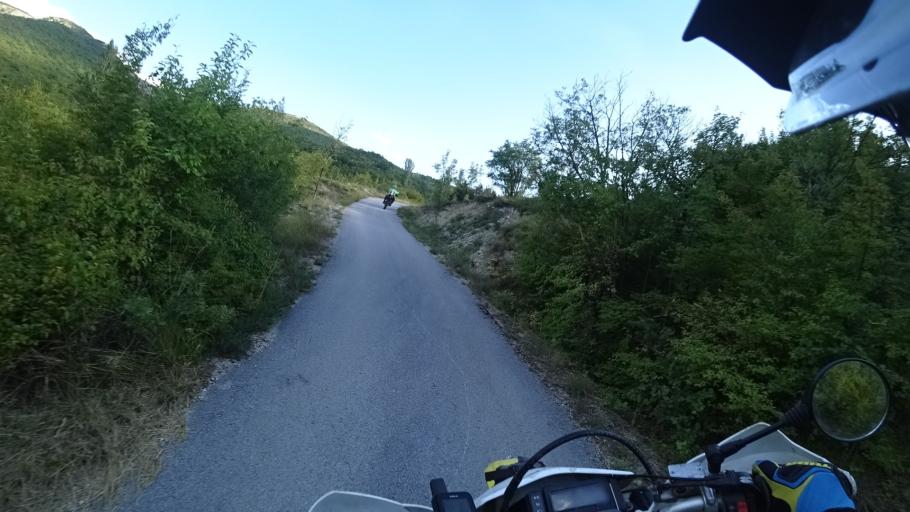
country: HR
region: Sibensko-Kniniska
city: Knin
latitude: 44.2036
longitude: 16.0690
